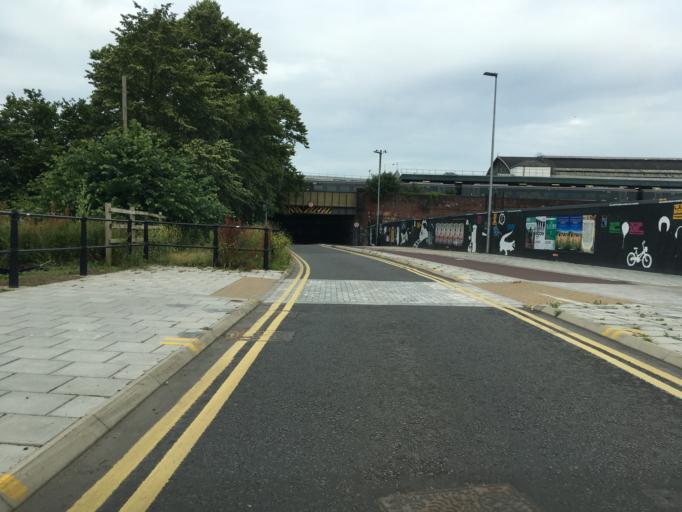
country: GB
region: England
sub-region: Bristol
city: Bristol
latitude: 51.4484
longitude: -2.5784
